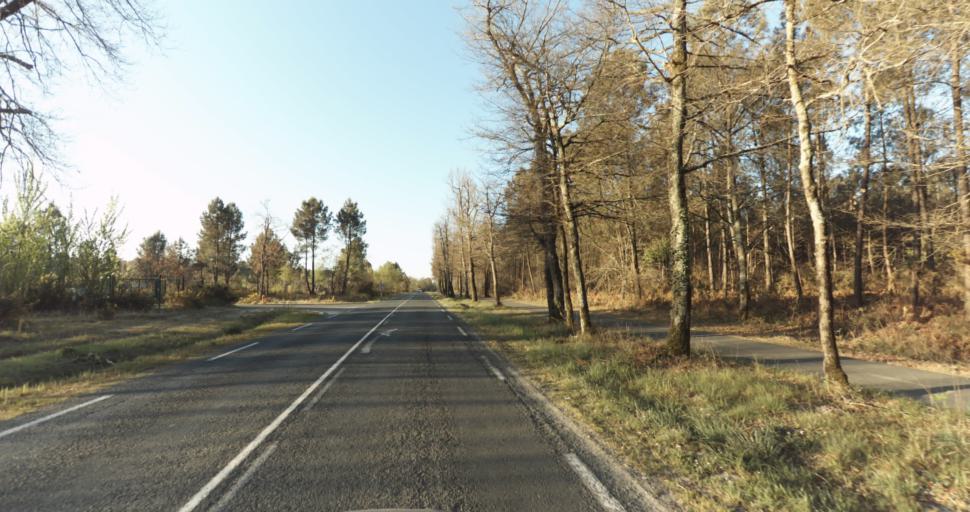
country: FR
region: Aquitaine
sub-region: Departement de la Gironde
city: Martignas-sur-Jalle
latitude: 44.8255
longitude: -0.7784
